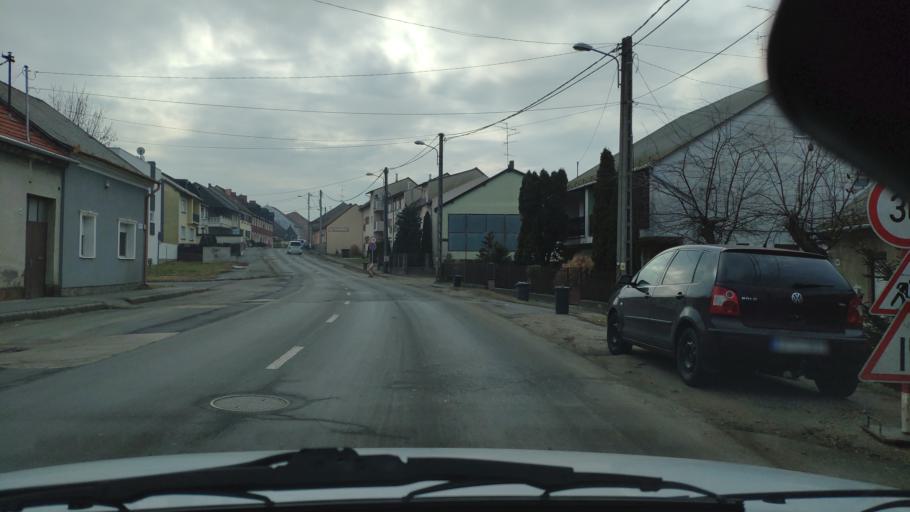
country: HU
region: Zala
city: Nagykanizsa
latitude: 46.4623
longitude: 16.9859
